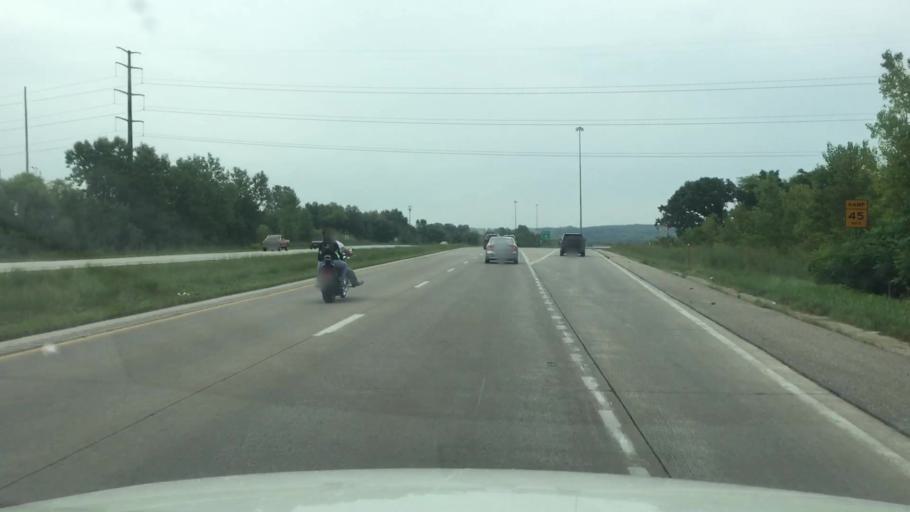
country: US
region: Iowa
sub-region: Warren County
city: Carlisle
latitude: 41.5107
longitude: -93.5766
